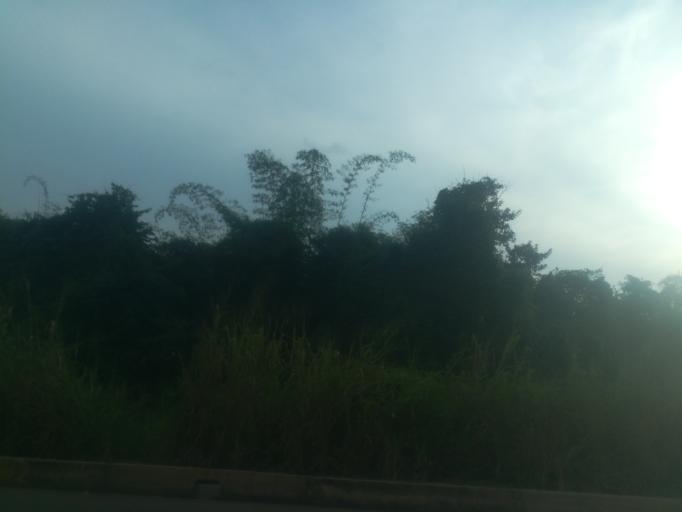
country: NG
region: Ogun
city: Abeokuta
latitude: 7.1610
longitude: 3.3207
